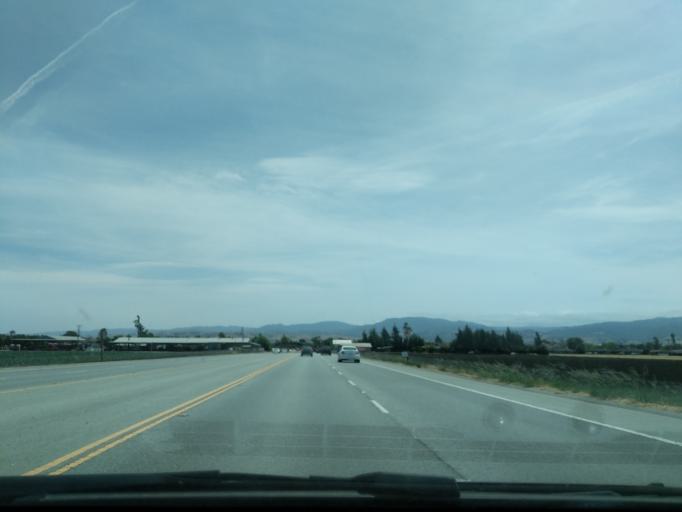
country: US
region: California
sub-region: San Benito County
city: Hollister
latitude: 36.8600
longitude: -121.3908
